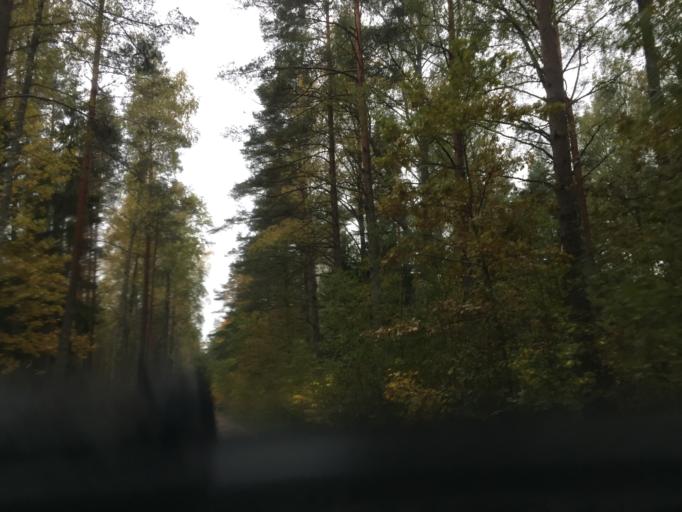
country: LV
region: Engure
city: Smarde
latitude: 56.9287
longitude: 23.4758
